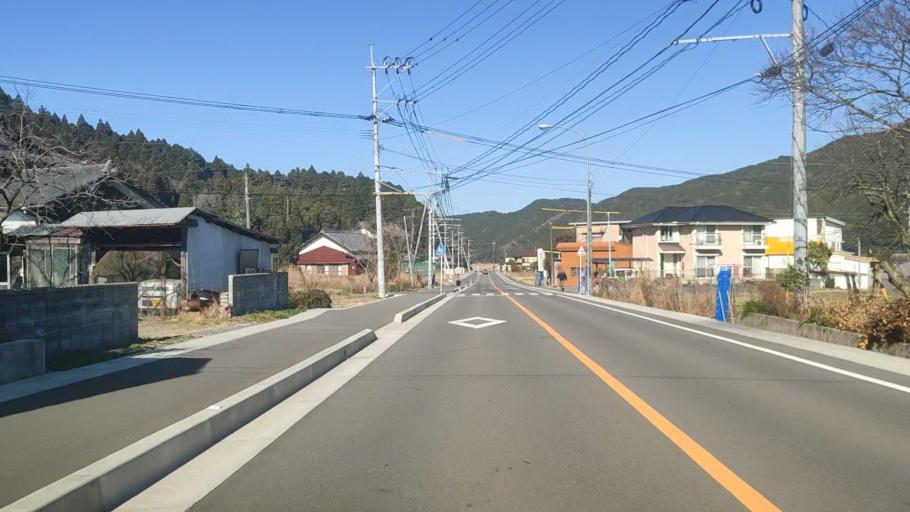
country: JP
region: Oita
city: Saiki
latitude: 32.9207
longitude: 131.9272
